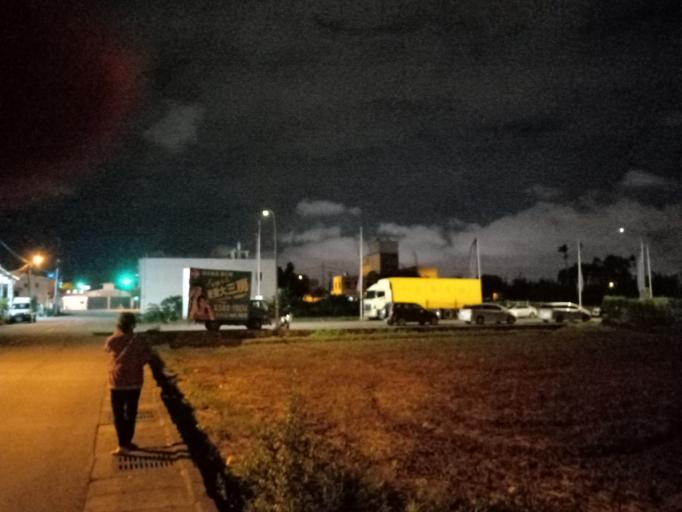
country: TW
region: Taiwan
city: Taoyuan City
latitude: 24.9436
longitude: 121.2591
